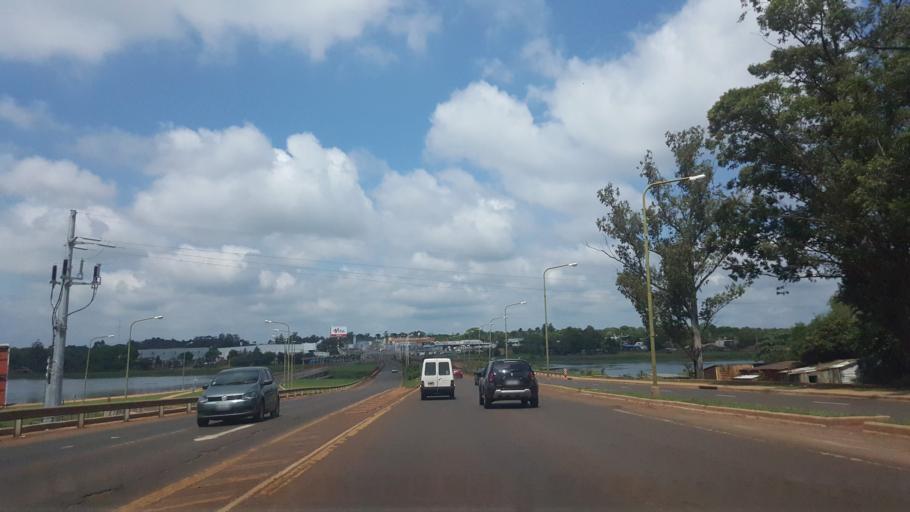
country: AR
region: Misiones
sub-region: Departamento de Capital
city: Posadas
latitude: -27.4167
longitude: -55.9005
